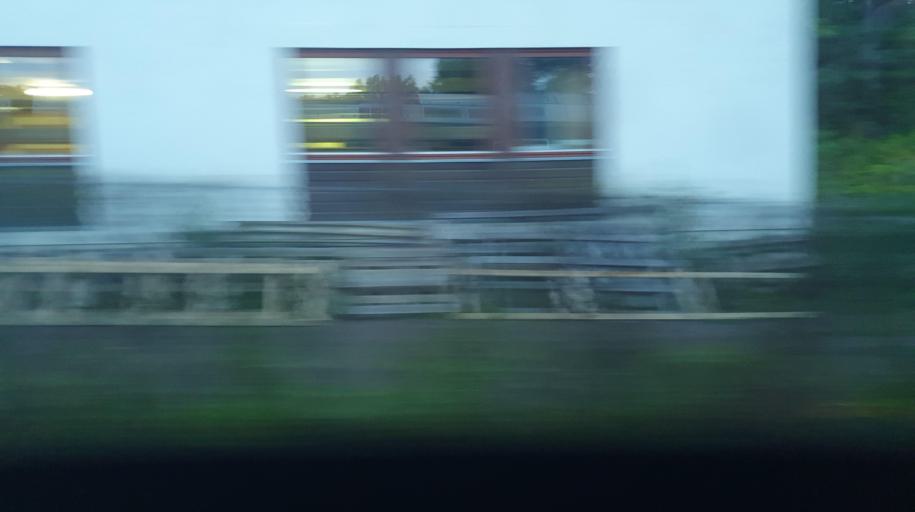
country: NO
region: Vestfold
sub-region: Horten
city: Skoppum
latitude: 59.3886
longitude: 10.4102
